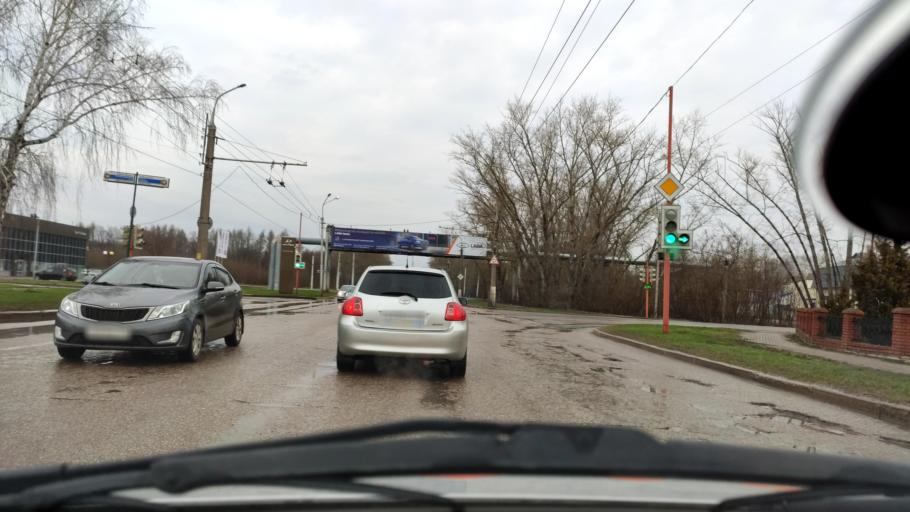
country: RU
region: Bashkortostan
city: Sterlitamak
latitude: 53.6549
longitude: 55.9485
